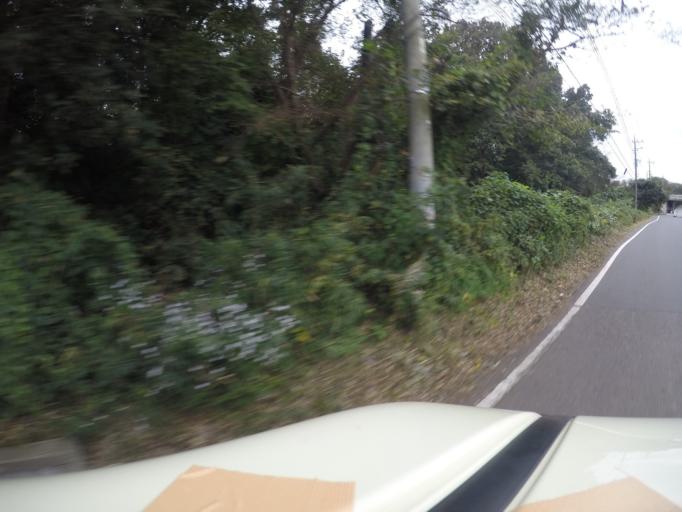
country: JP
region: Ibaraki
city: Naka
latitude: 36.0638
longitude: 140.1590
